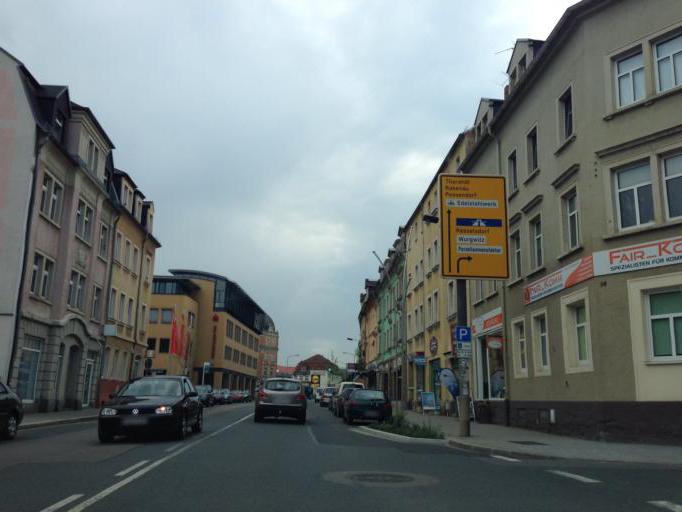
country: DE
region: Saxony
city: Freital
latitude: 51.0093
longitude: 13.6602
